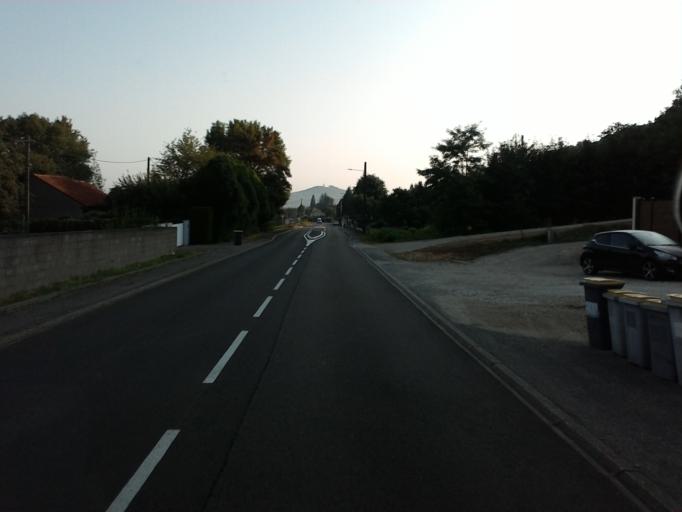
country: FR
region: Franche-Comte
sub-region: Departement de la Haute-Saone
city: Echenoz-la-Meline
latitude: 47.5977
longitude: 6.1403
